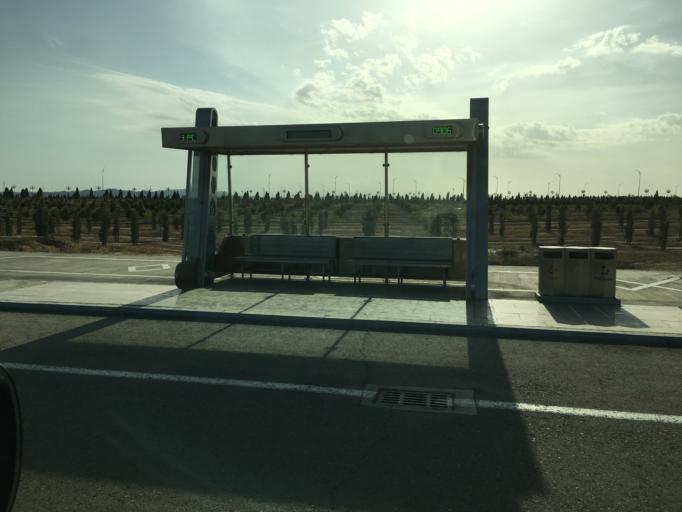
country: TM
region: Balkan
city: Turkmenbasy
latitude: 39.9566
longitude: 52.8644
